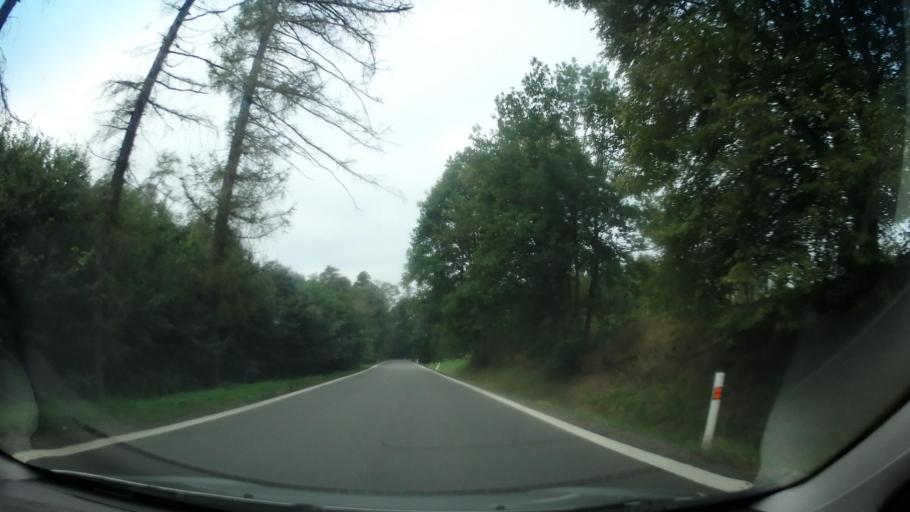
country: CZ
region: Central Bohemia
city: Bystrice
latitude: 49.7595
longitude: 14.6417
